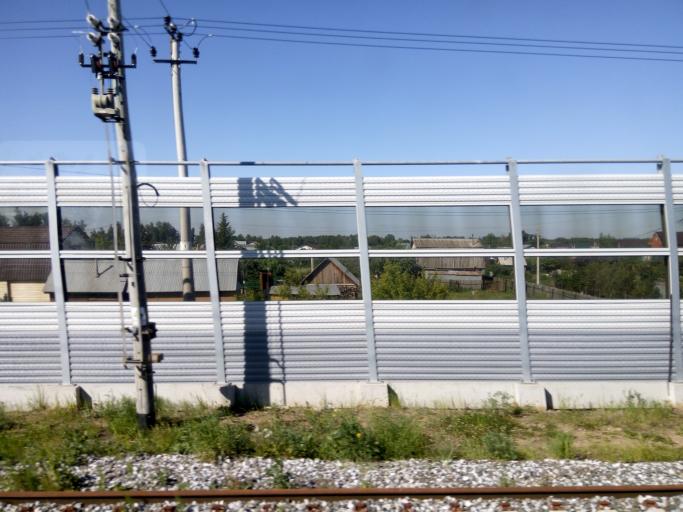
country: RU
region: Tatarstan
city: Stolbishchi
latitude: 55.6700
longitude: 49.2146
